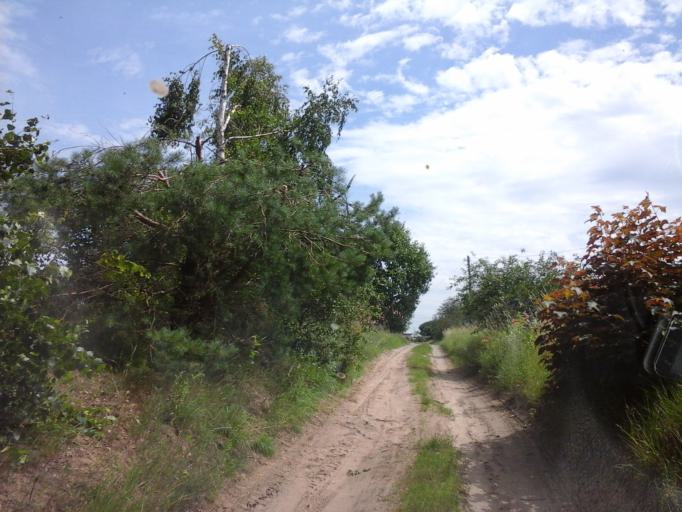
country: PL
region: Lubusz
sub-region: Powiat strzelecko-drezdenecki
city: Dobiegniew
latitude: 53.0557
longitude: 15.7577
